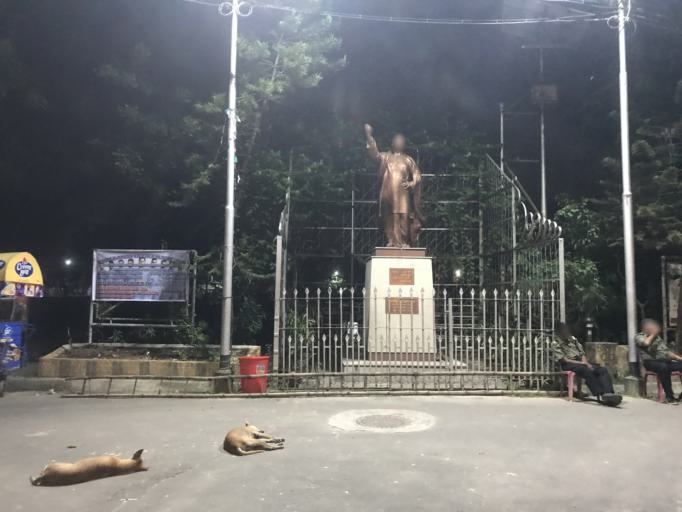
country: IN
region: West Bengal
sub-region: Kolkata
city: Kolkata
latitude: 22.6002
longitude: 88.3767
